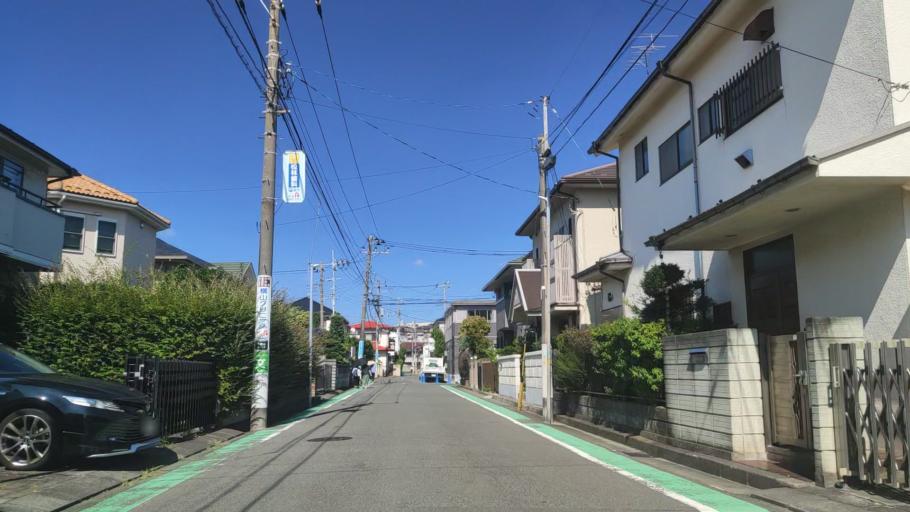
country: JP
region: Kanagawa
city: Yokohama
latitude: 35.5198
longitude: 139.6264
